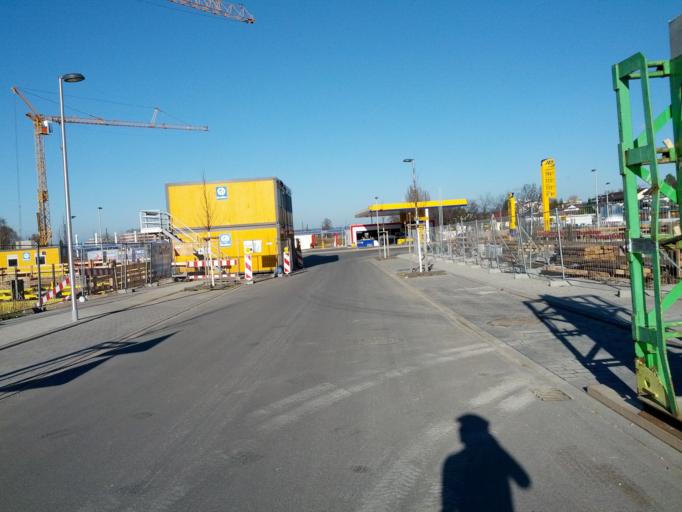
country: DE
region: Baden-Wuerttemberg
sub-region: Freiburg Region
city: Freiburg
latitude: 48.0146
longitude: 7.8502
